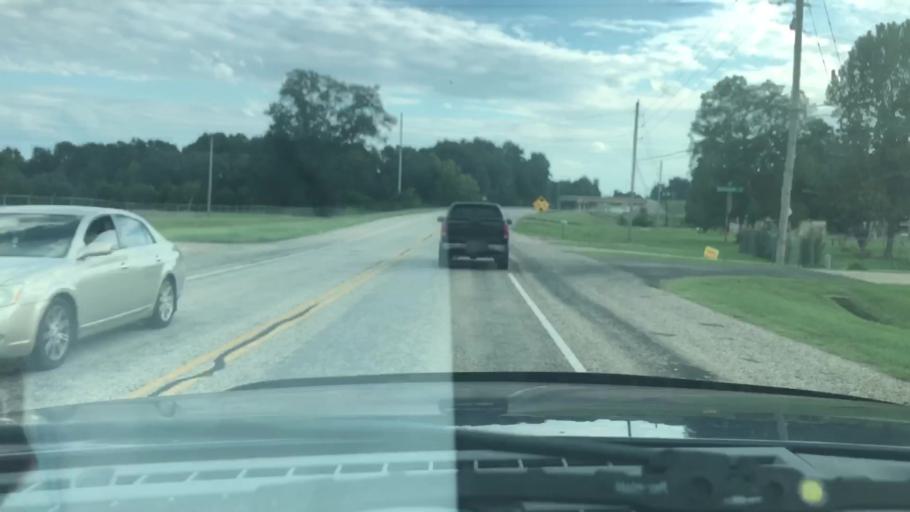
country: US
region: Texas
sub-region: Bowie County
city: Texarkana
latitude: 33.3903
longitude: -94.0657
